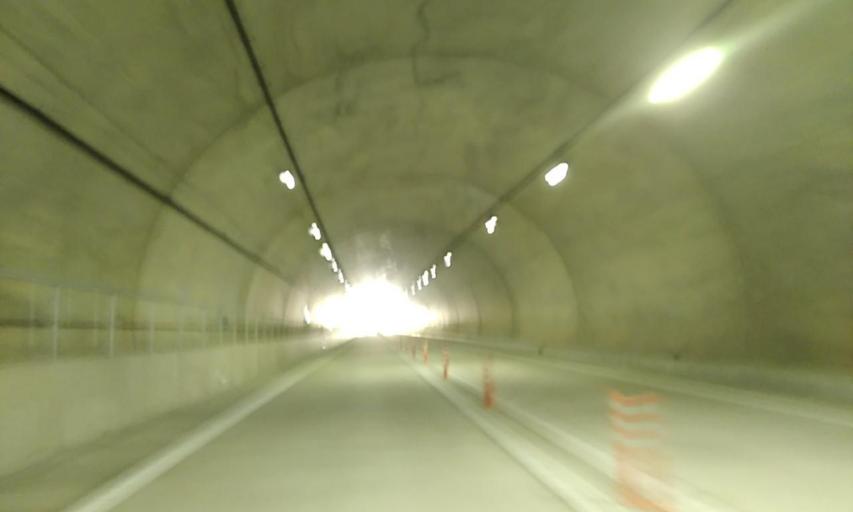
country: JP
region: Mie
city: Owase
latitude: 34.0681
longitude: 136.1732
